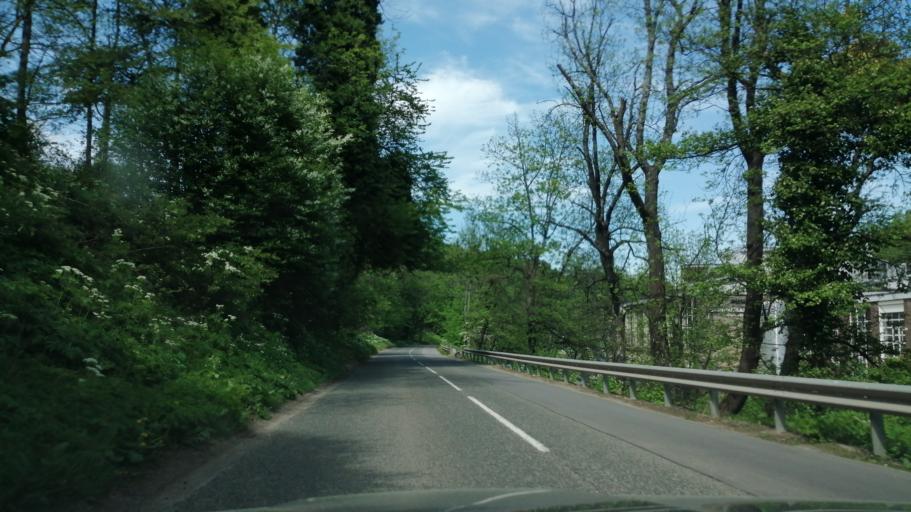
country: GB
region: Scotland
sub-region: Moray
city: Dufftown
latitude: 57.4469
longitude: -3.1177
